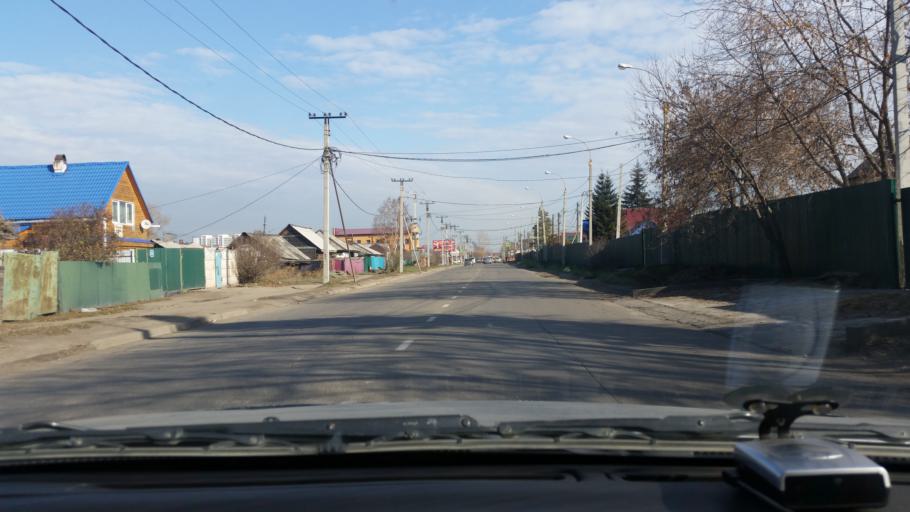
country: RU
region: Irkutsk
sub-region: Irkutskiy Rayon
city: Irkutsk
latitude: 52.2840
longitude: 104.3265
